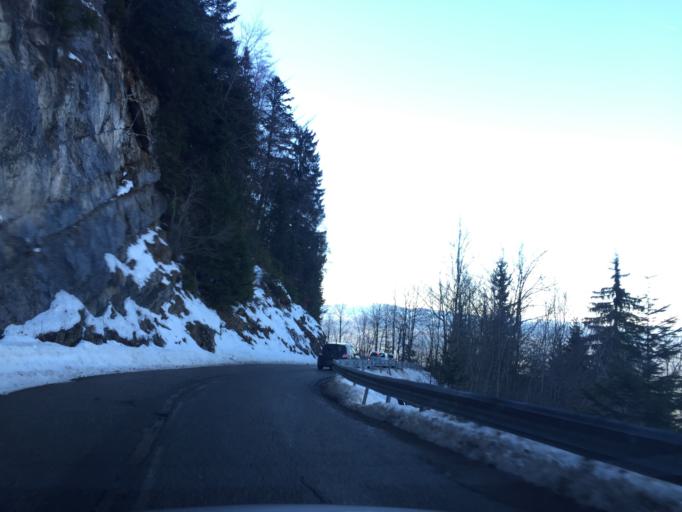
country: FR
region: Rhone-Alpes
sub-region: Departement de la Haute-Savoie
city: Cusy
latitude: 45.6982
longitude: 6.0096
